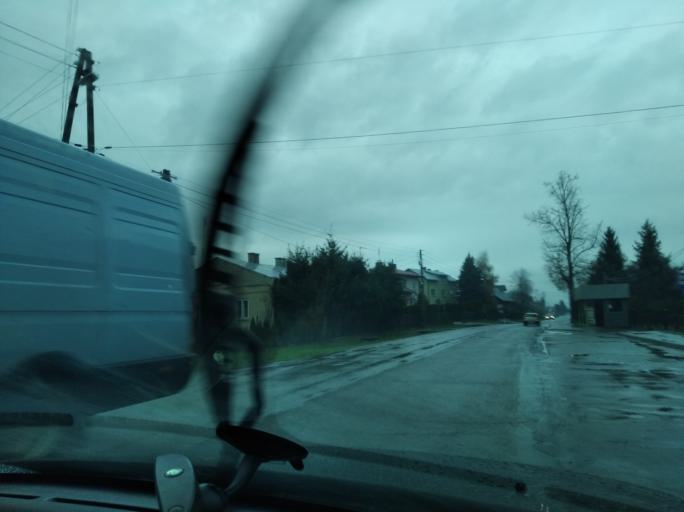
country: PL
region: Subcarpathian Voivodeship
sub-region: Powiat lancucki
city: Albigowa
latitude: 50.0173
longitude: 22.2249
